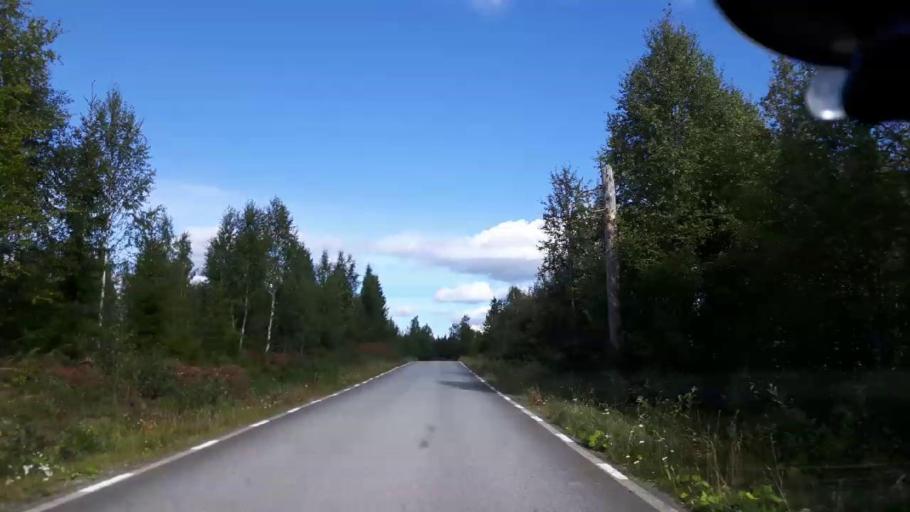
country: SE
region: Jaemtland
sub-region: OEstersunds Kommun
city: Brunflo
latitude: 63.1957
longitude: 15.2211
